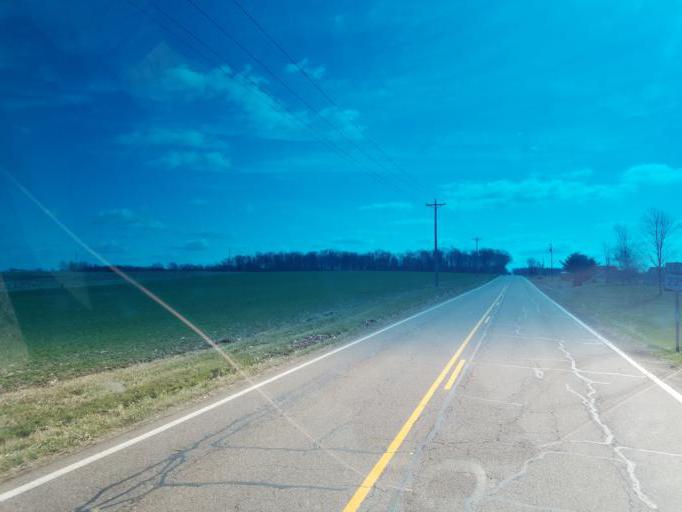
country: US
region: Ohio
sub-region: Knox County
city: Gambier
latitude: 40.3587
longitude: -82.3624
